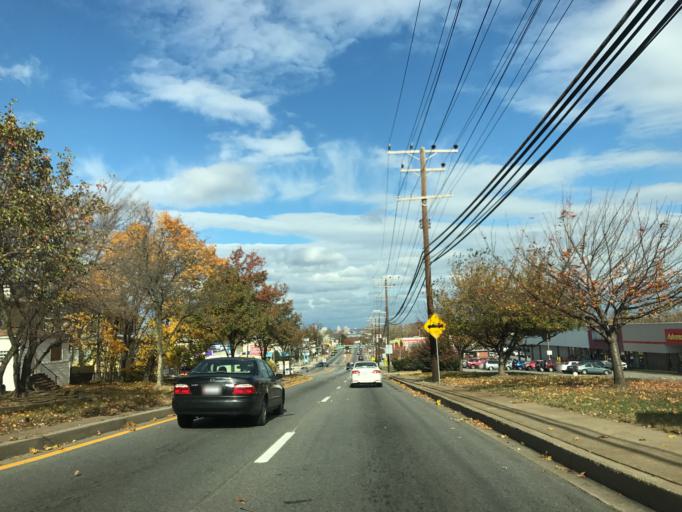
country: US
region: Maryland
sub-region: Anne Arundel County
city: Brooklyn Park
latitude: 39.2223
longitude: -76.6137
